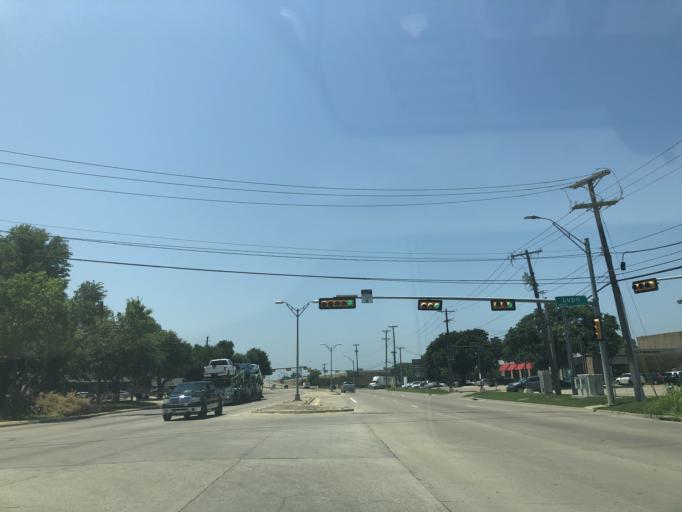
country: US
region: Texas
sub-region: Dallas County
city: Dallas
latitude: 32.8076
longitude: -96.8517
